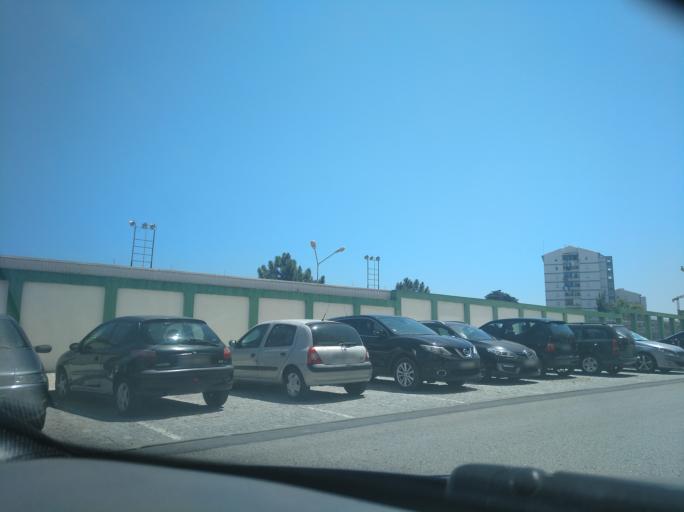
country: PT
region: Lisbon
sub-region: Loures
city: Moscavide
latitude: 38.7742
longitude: -9.1036
